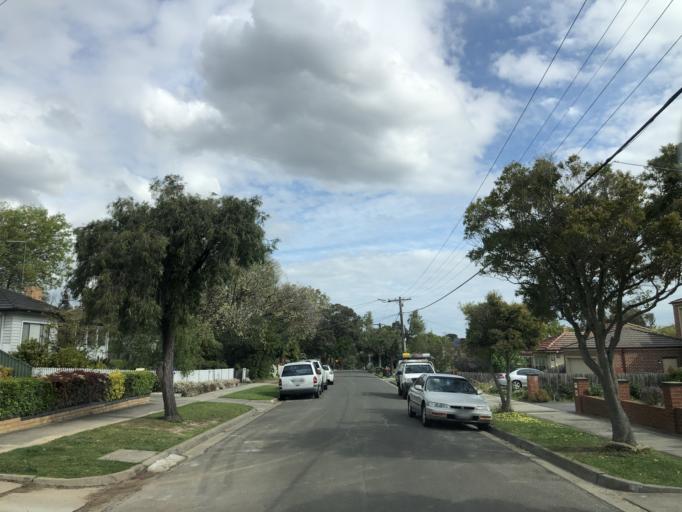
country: AU
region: Victoria
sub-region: Monash
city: Ashwood
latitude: -37.8641
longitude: 145.1085
